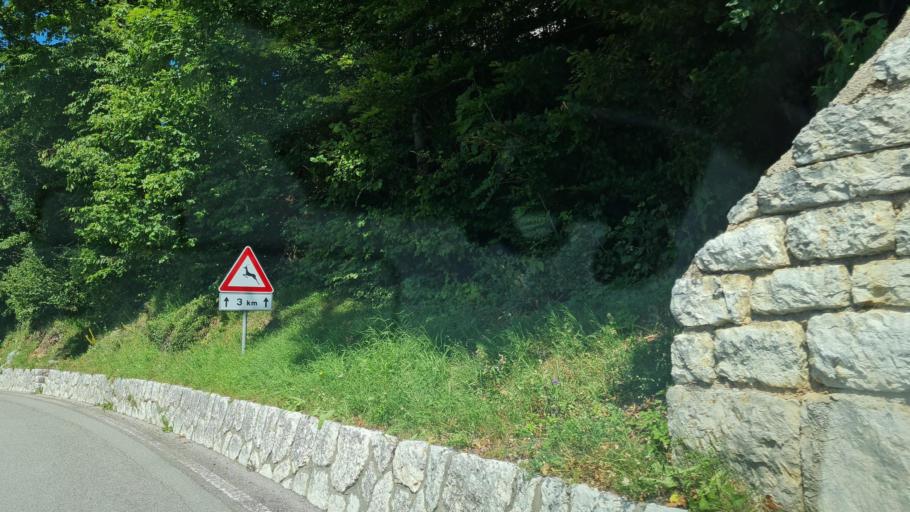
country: IT
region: Trentino-Alto Adige
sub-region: Provincia di Trento
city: Terragnolo
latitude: 45.8973
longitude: 11.1552
